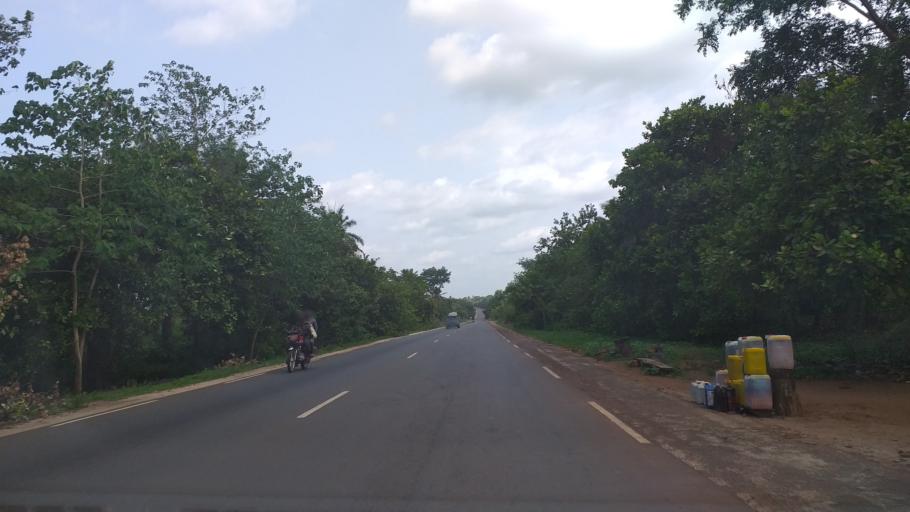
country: GN
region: Boke
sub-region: Boke Prefecture
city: Sangueya
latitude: 10.7417
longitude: -14.3792
